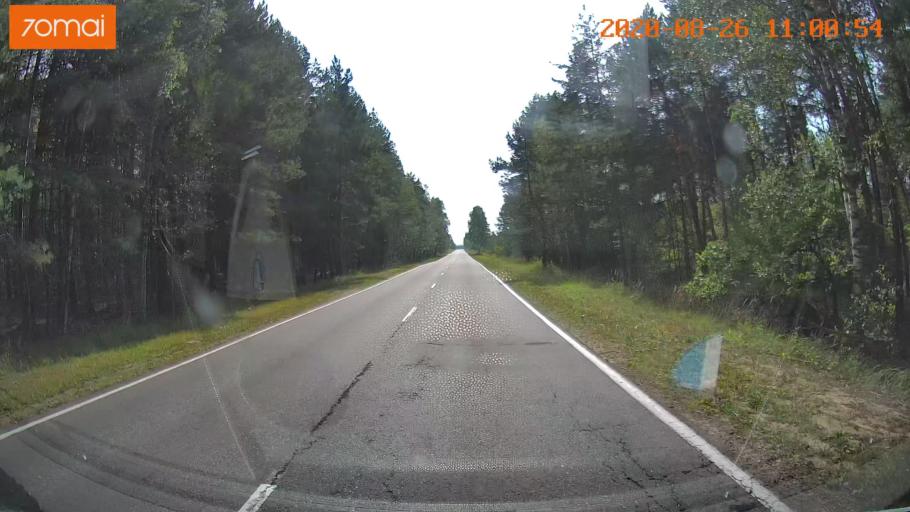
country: RU
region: Rjazan
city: Izhevskoye
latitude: 54.5696
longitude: 41.2182
